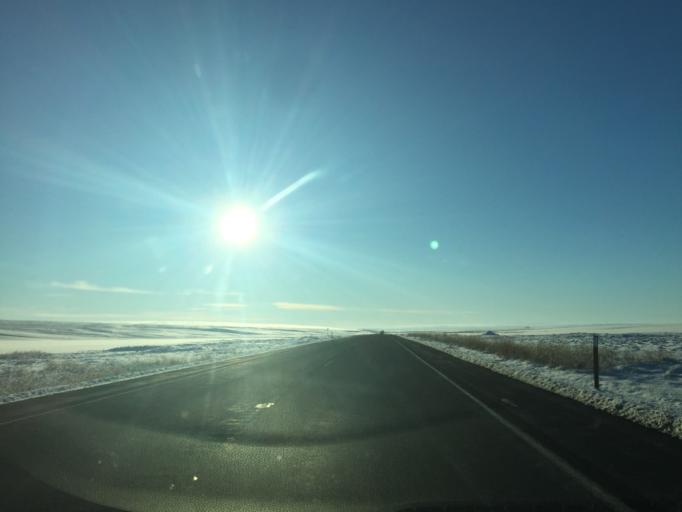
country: US
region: Washington
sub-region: Okanogan County
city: Coulee Dam
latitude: 47.6884
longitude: -118.9786
